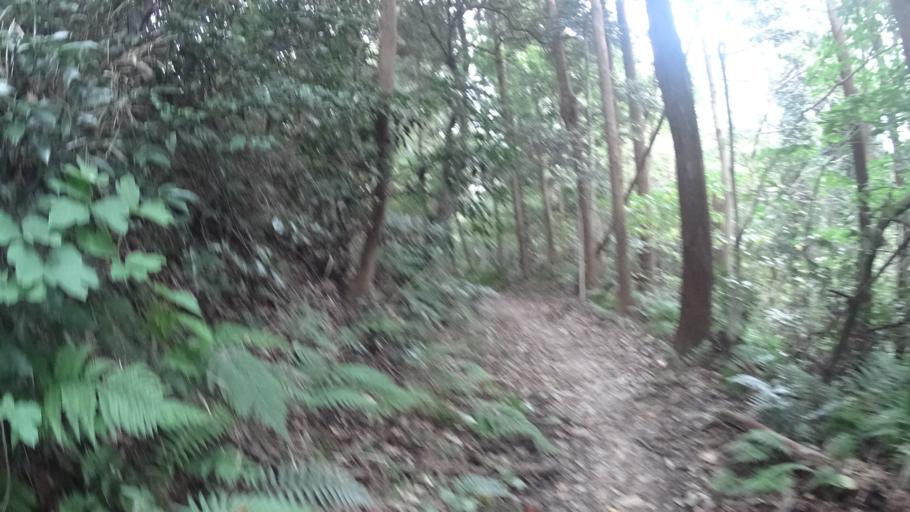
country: JP
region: Kanagawa
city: Zushi
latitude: 35.2914
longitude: 139.6051
